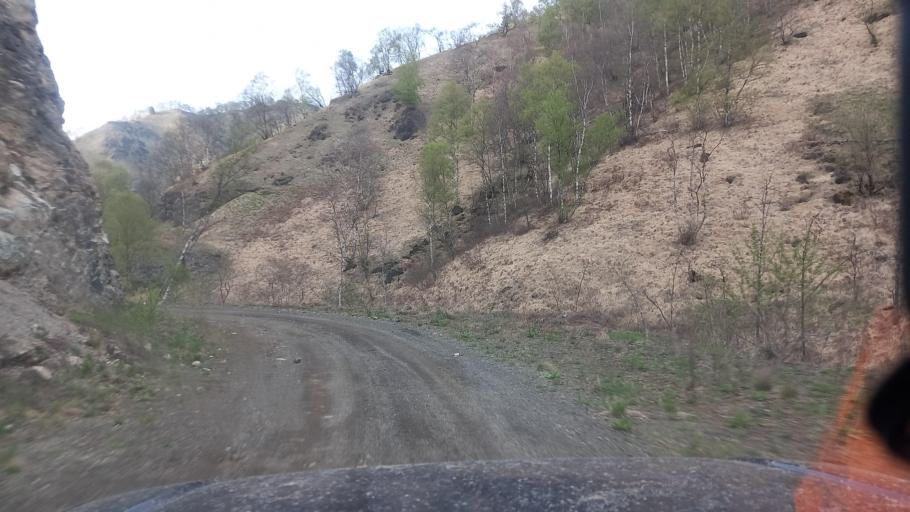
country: RU
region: Kabardino-Balkariya
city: Kamennomostskoye
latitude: 43.7071
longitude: 42.8459
